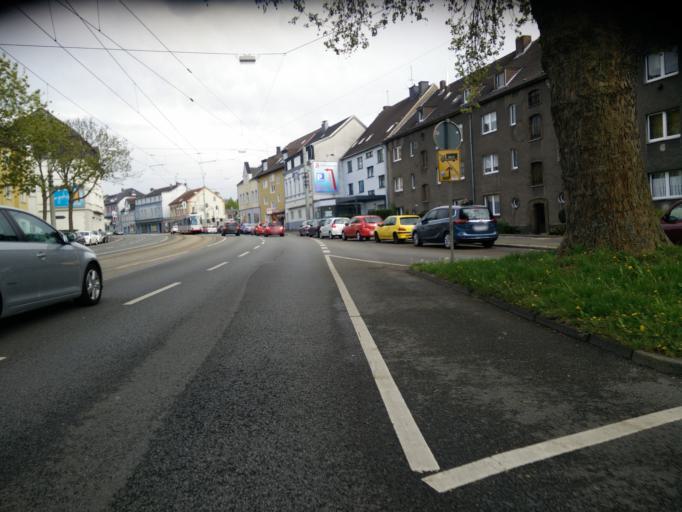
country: DE
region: North Rhine-Westphalia
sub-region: Regierungsbezirk Arnsberg
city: Bochum
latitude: 51.4722
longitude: 7.2439
